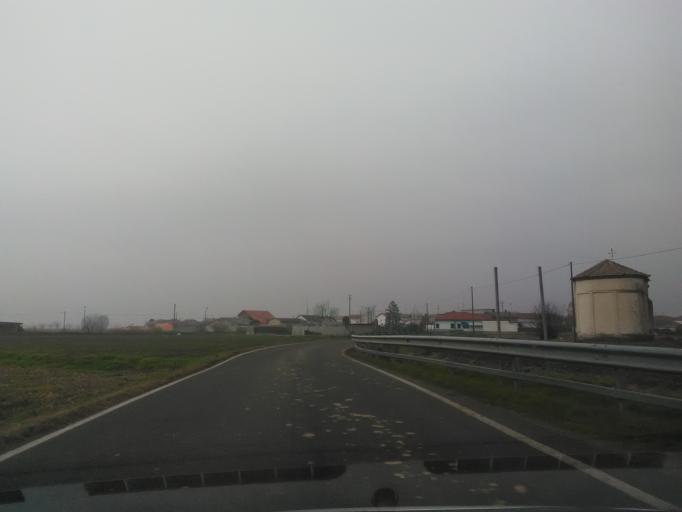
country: IT
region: Piedmont
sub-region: Provincia di Vercelli
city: Tronzano Vercellese
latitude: 45.3388
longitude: 8.1824
